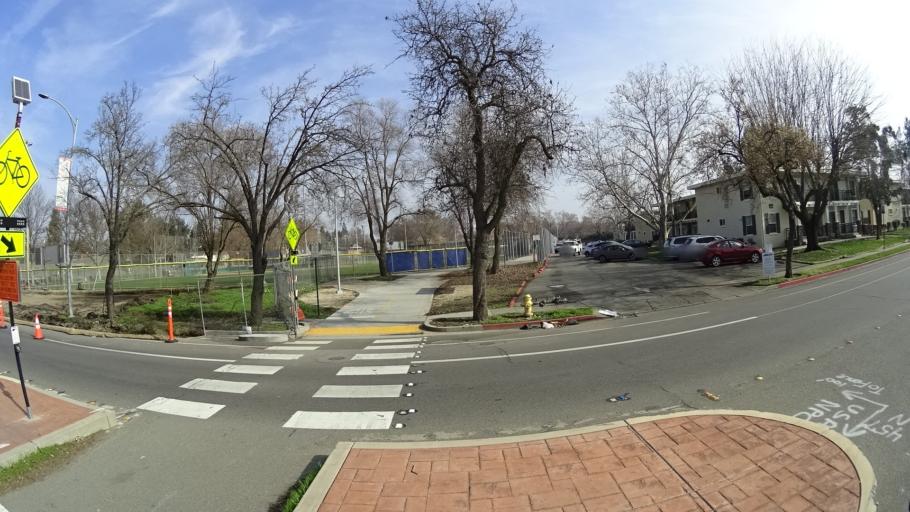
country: US
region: California
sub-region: Yolo County
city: Davis
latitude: 38.5594
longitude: -121.7448
